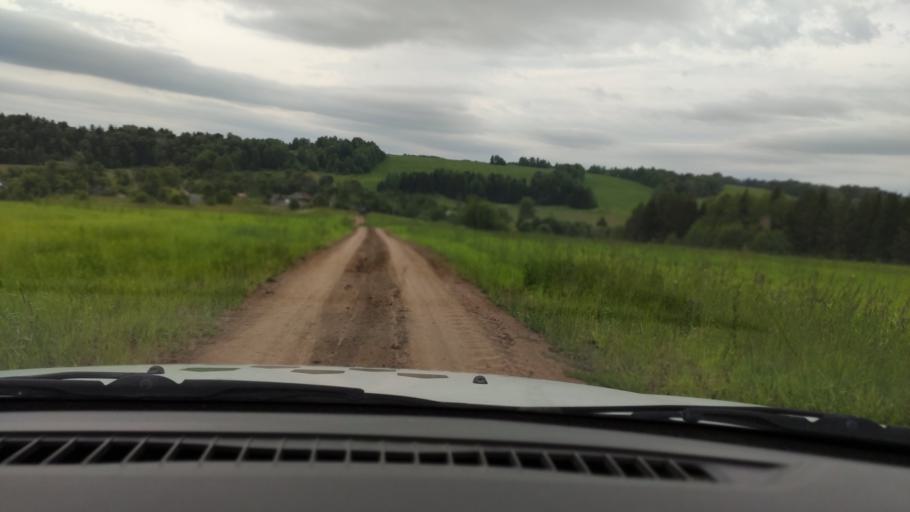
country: RU
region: Perm
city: Orda
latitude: 57.2951
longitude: 56.5943
